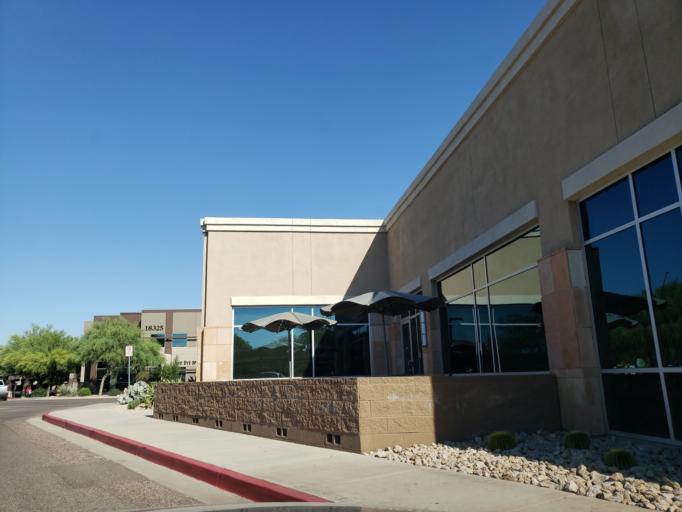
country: US
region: Arizona
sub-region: Maricopa County
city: Paradise Valley
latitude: 33.6533
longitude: -111.9303
